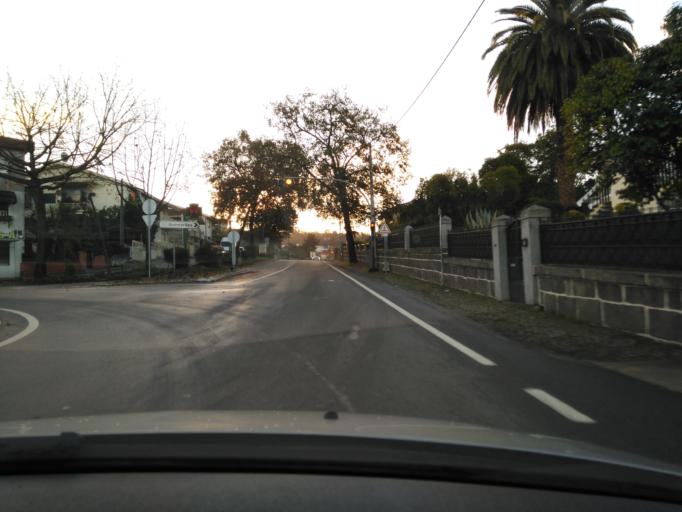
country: PT
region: Braga
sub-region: Guimaraes
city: Ponte
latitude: 41.4604
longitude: -8.3135
